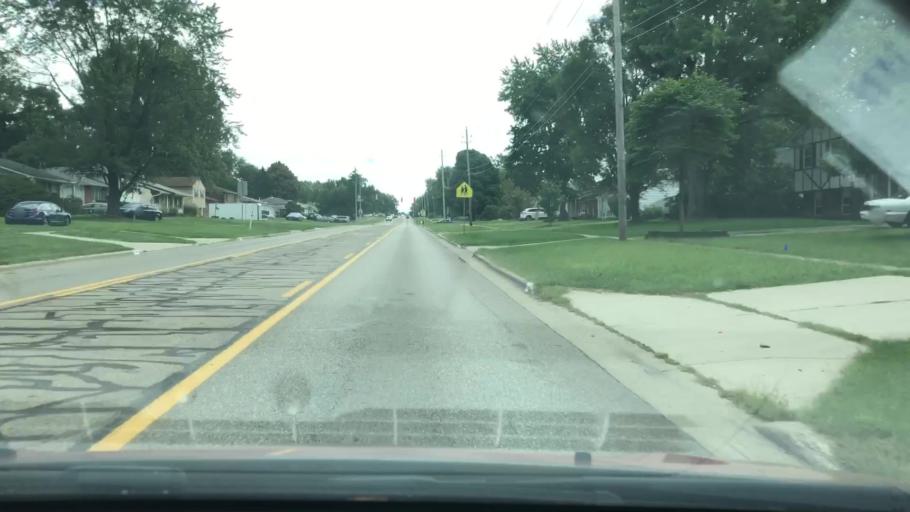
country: US
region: Ohio
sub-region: Franklin County
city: Huber Ridge
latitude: 40.0955
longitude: -82.9212
